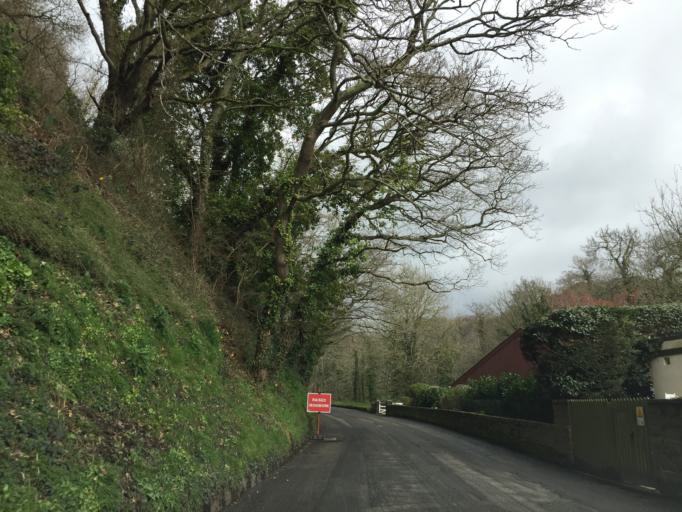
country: JE
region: St Helier
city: Saint Helier
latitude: 49.2199
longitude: -2.1748
